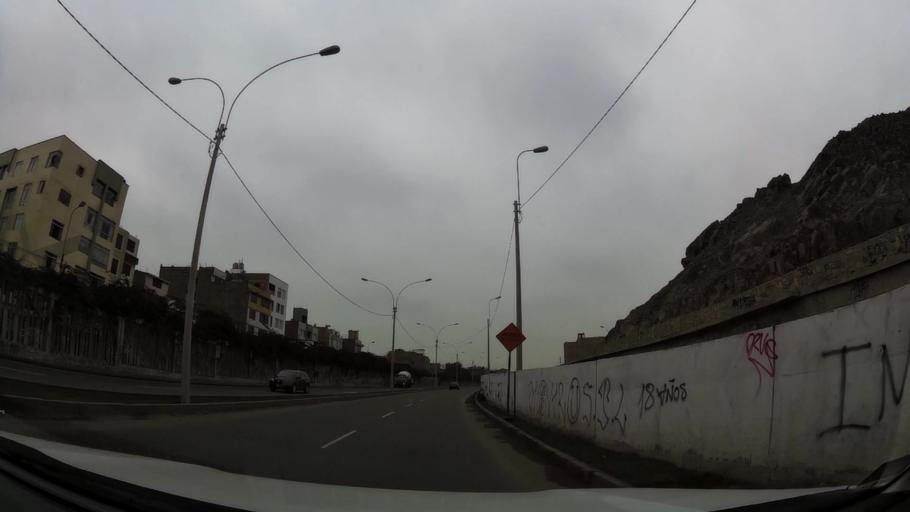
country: PE
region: Lima
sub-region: Lima
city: Vitarte
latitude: -12.0520
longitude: -76.9378
